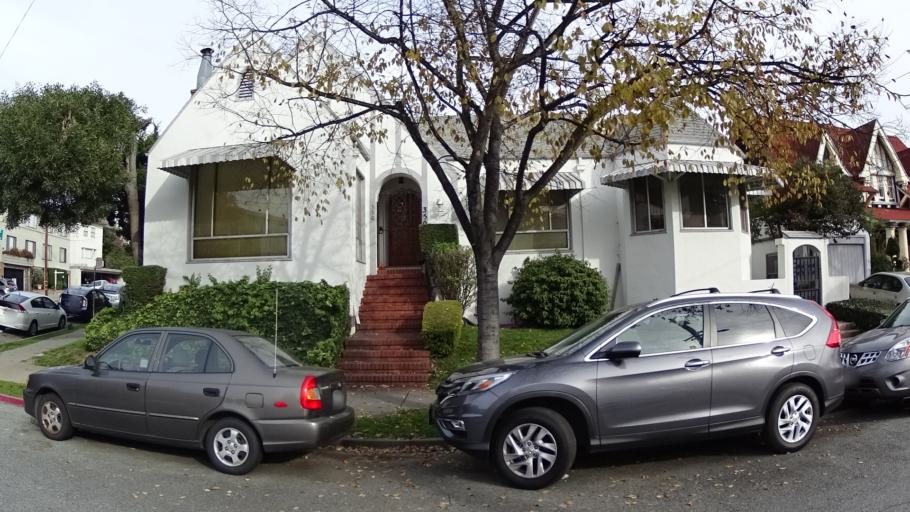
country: US
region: California
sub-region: Alameda County
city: Oakland
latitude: 37.8125
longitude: -122.2534
